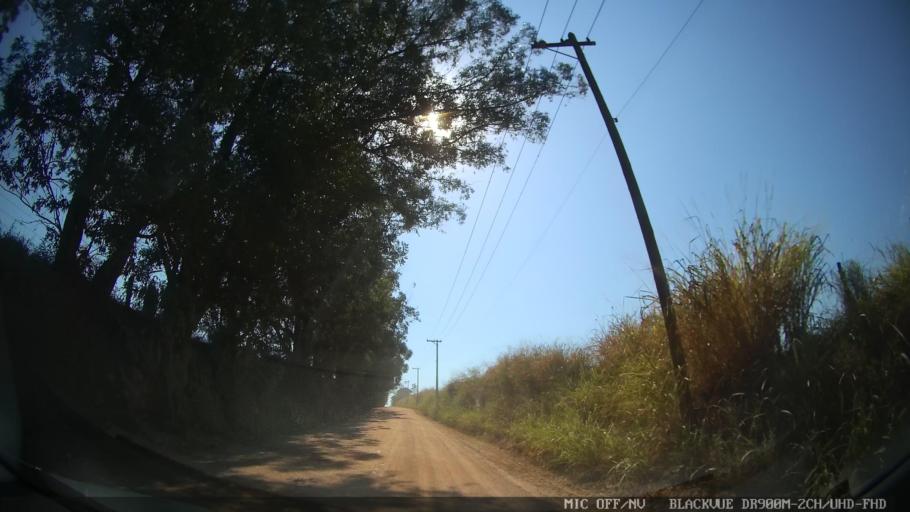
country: BR
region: Sao Paulo
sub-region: Itupeva
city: Itupeva
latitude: -23.1147
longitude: -47.0859
